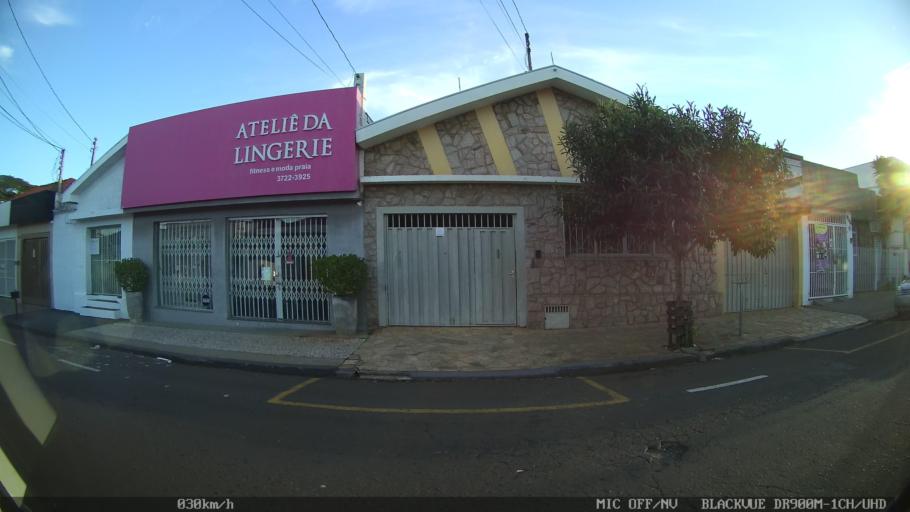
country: BR
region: Sao Paulo
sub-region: Franca
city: Franca
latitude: -20.5287
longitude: -47.3919
